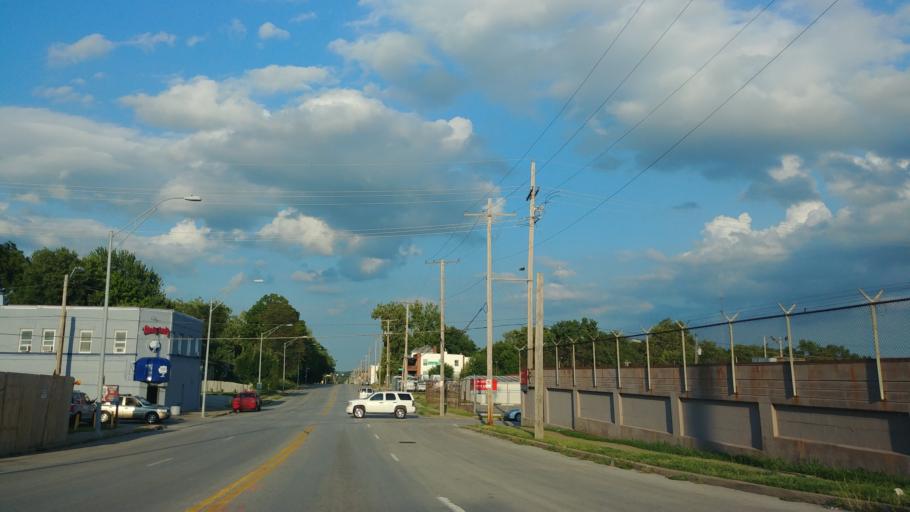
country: US
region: Missouri
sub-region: Jackson County
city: Kansas City
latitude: 39.0990
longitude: -94.5501
